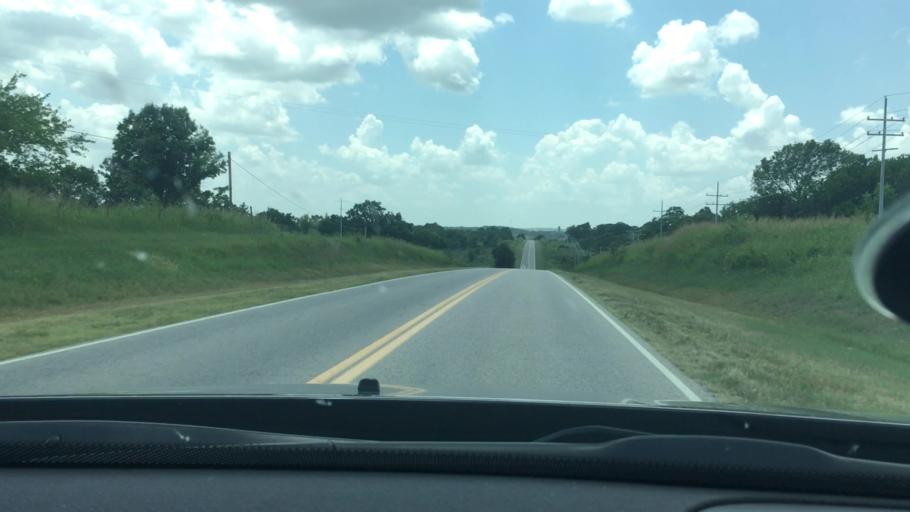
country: US
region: Oklahoma
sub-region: Pontotoc County
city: Ada
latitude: 34.6311
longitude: -96.6349
